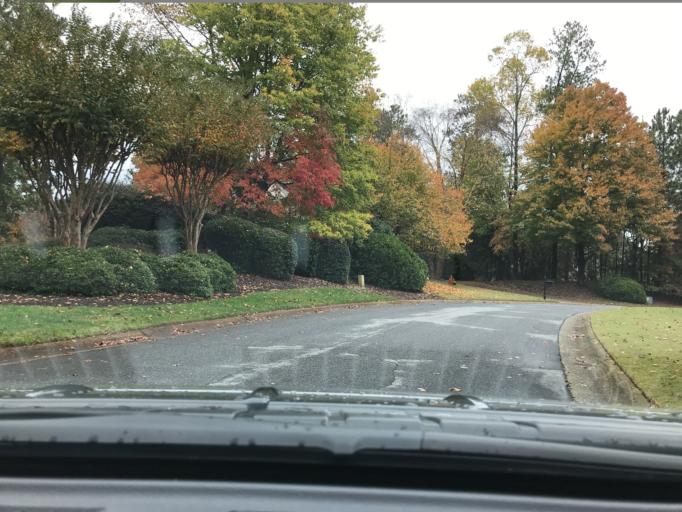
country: US
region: Georgia
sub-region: Fulton County
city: Johns Creek
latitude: 34.0168
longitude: -84.2459
